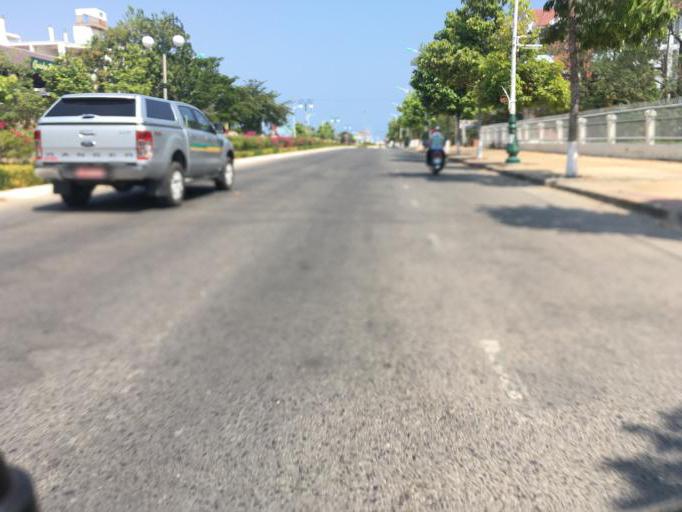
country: VN
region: Ninh Thuan
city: Phan Rang-Thap Cham
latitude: 11.5631
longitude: 109.0188
